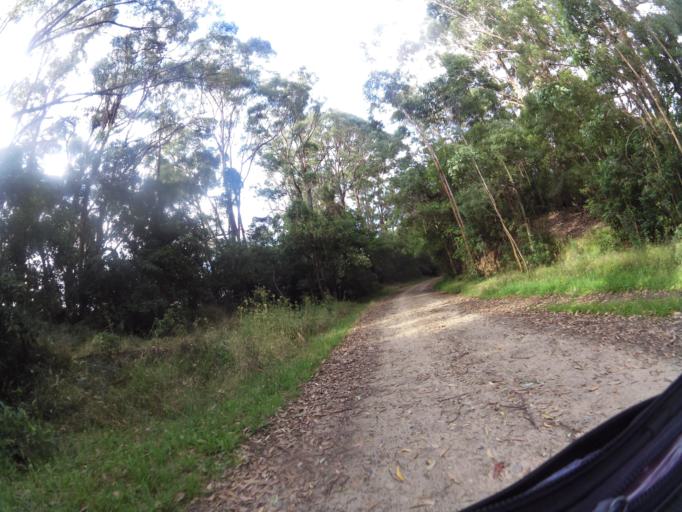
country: AU
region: Victoria
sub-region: East Gippsland
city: Lakes Entrance
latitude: -37.7344
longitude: 148.4267
